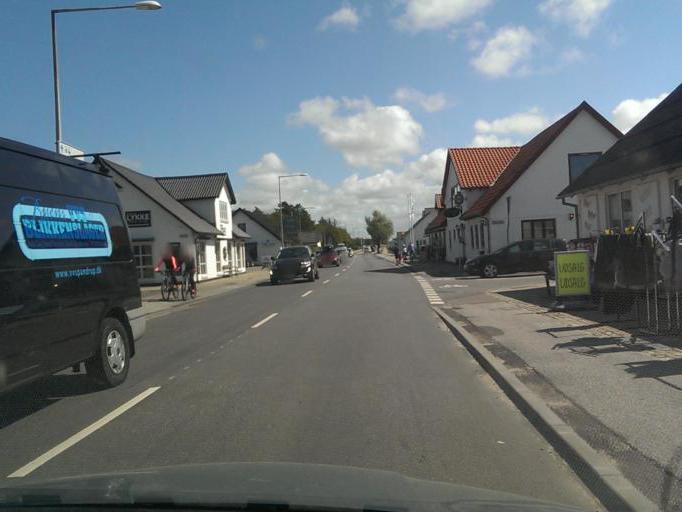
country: DK
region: North Denmark
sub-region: Jammerbugt Kommune
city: Pandrup
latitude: 57.2486
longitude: 9.6156
